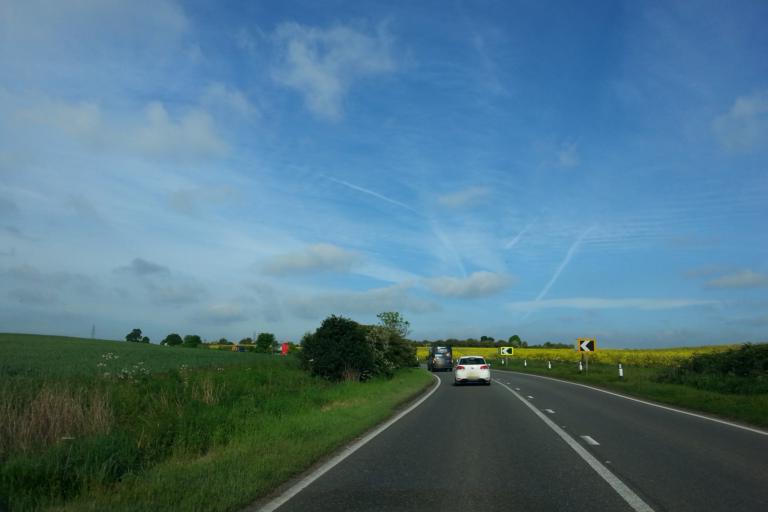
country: GB
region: England
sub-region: Nottinghamshire
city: Bilsthorpe
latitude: 53.1229
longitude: -1.0286
